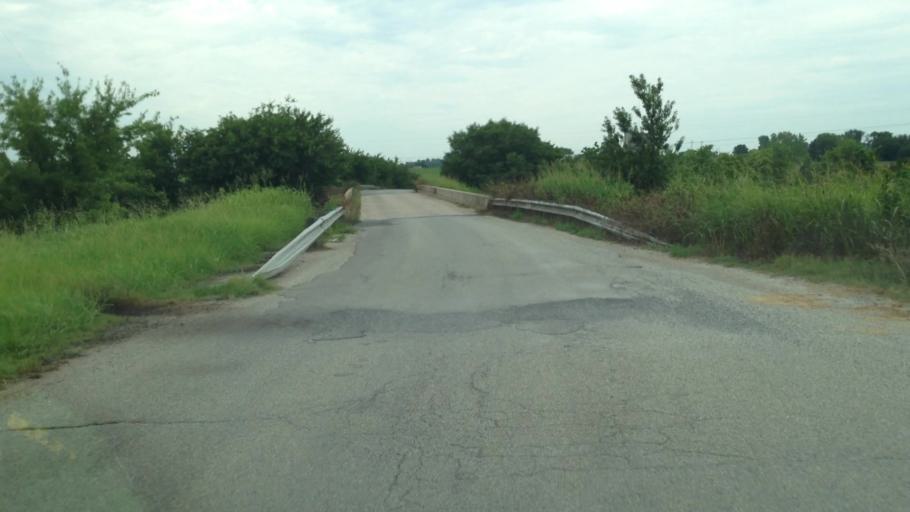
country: US
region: Oklahoma
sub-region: Craig County
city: Vinita
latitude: 36.6379
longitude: -95.1251
